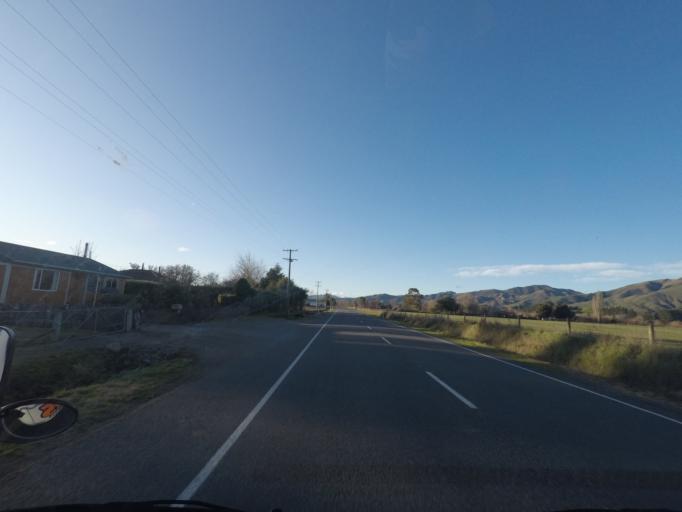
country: NZ
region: Canterbury
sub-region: Kaikoura District
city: Kaikoura
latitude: -42.7152
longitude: 173.2893
